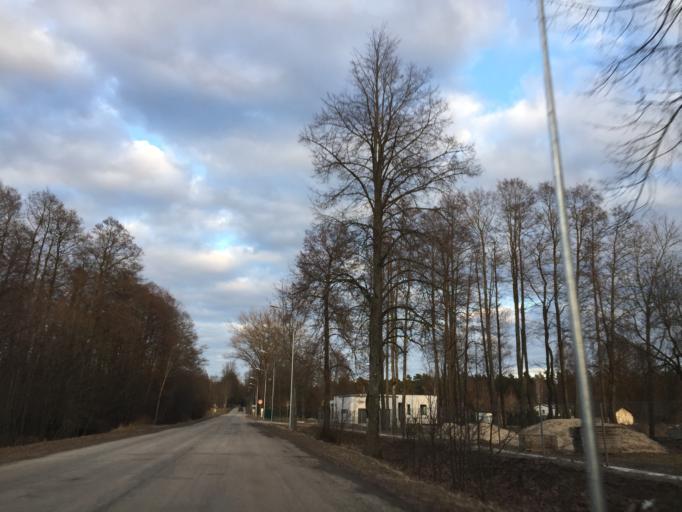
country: LV
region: Babite
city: Pinki
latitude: 56.9206
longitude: 23.8699
